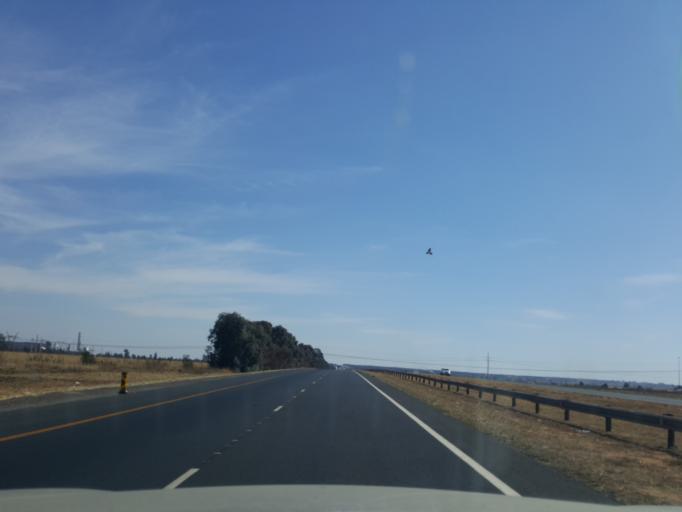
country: ZA
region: Mpumalanga
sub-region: Nkangala District Municipality
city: Witbank
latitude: -25.8725
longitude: 29.1091
